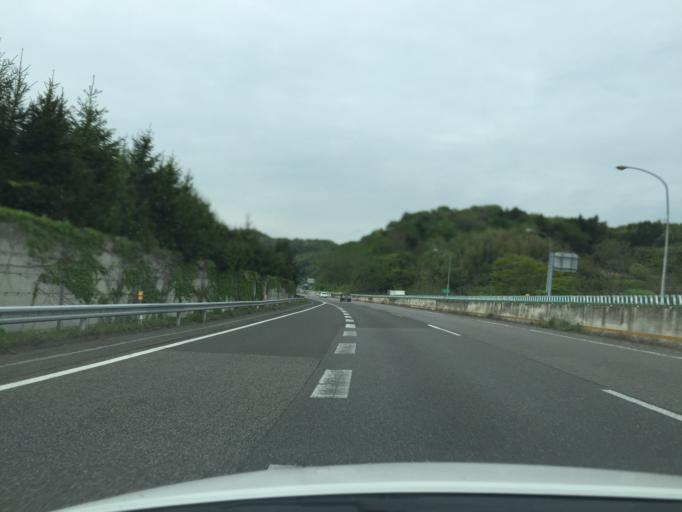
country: JP
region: Fukushima
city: Nihommatsu
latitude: 37.5920
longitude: 140.4187
